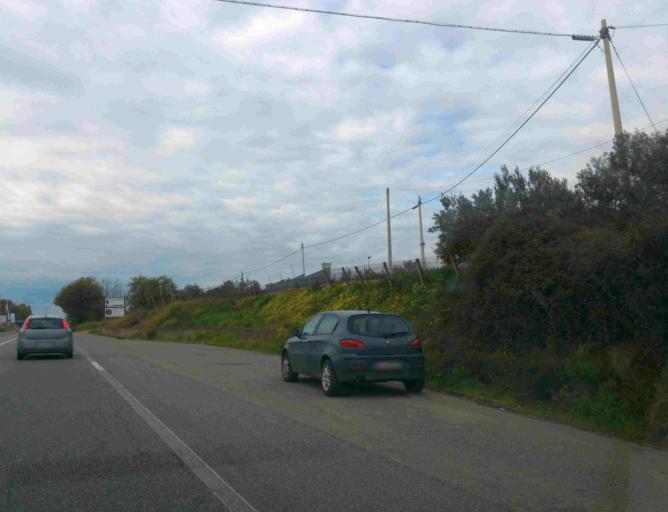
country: IT
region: Calabria
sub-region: Provincia di Catanzaro
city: Sellia Marina
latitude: 38.8916
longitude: 16.7209
